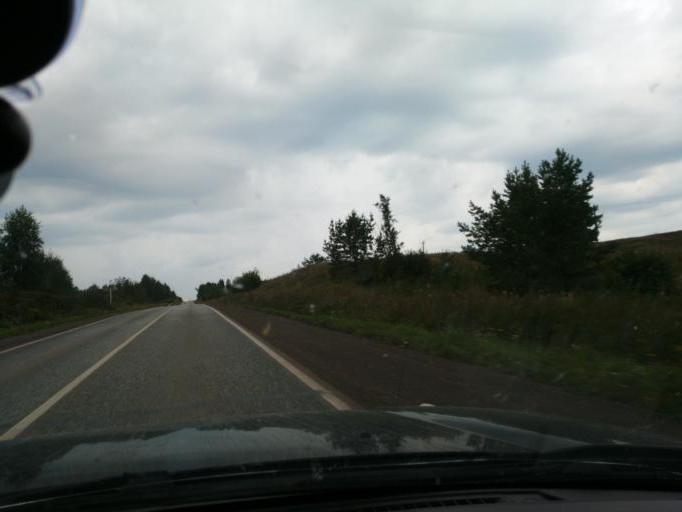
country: RU
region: Perm
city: Chernushka
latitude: 56.8432
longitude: 55.9764
